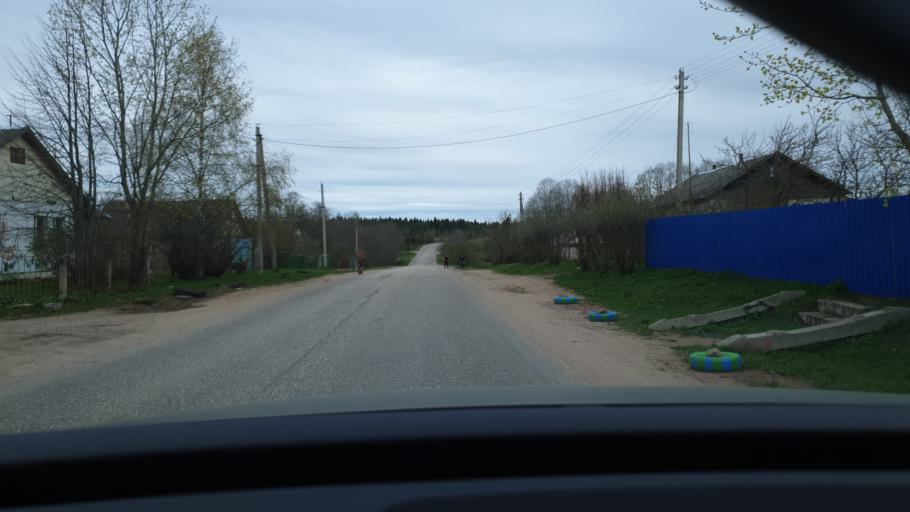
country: RU
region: Tverskaya
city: Berezayka
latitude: 58.0467
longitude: 33.7777
